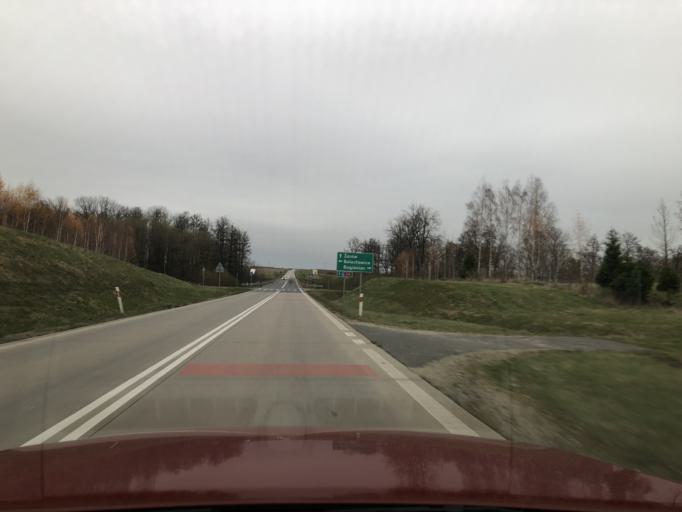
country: PL
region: Lower Silesian Voivodeship
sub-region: Powiat swidnicki
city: Swidnica
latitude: 50.8890
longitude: 16.4776
